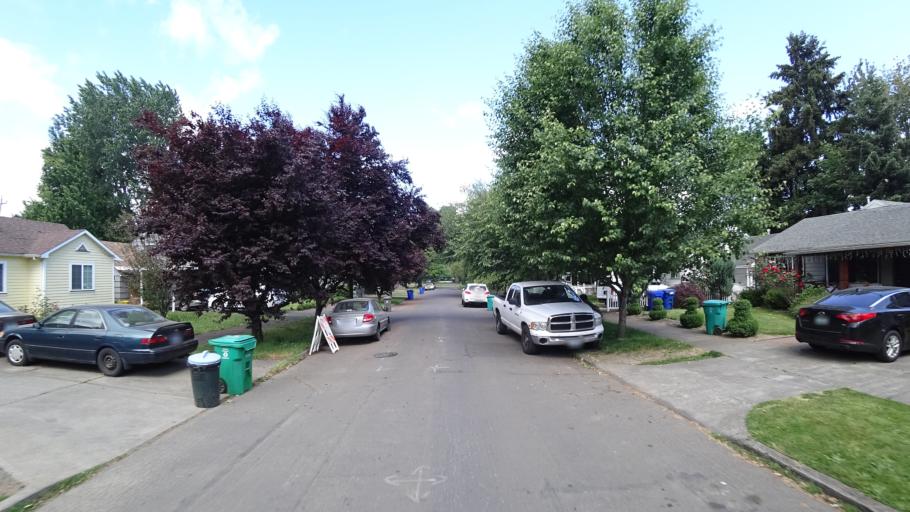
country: US
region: Oregon
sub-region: Washington County
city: West Haven
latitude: 45.6008
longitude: -122.7617
